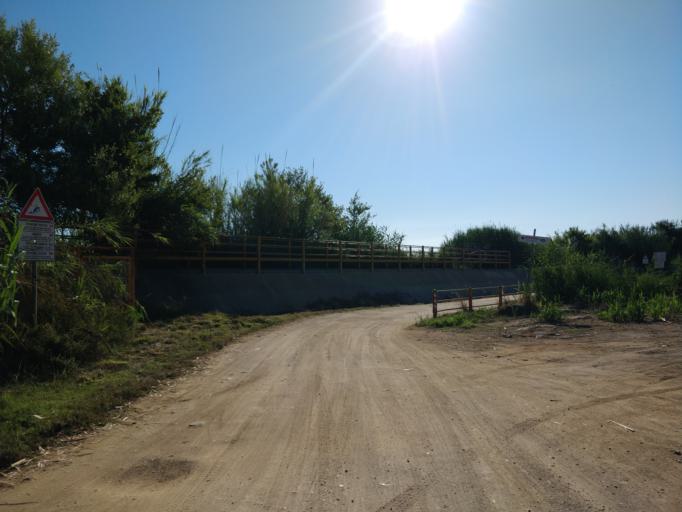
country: IT
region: Sardinia
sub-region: Provincia di Ogliastra
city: Lotzorai
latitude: 39.9597
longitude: 9.6824
